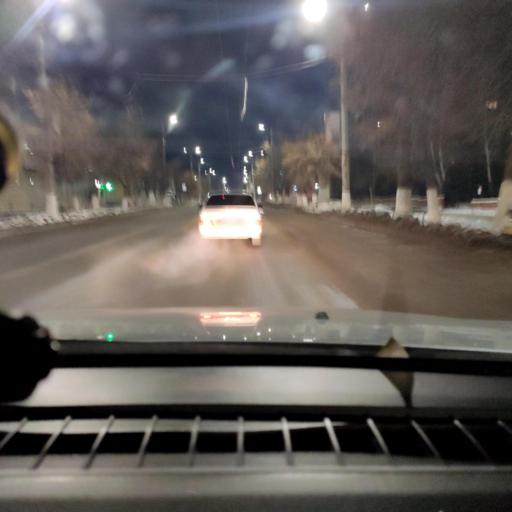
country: RU
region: Samara
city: Novokuybyshevsk
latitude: 53.0883
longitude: 49.9504
